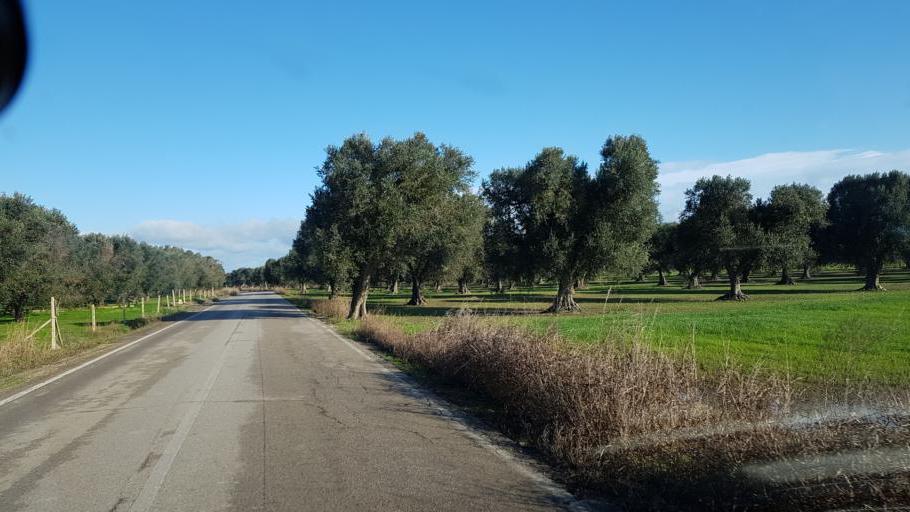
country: IT
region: Apulia
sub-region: Provincia di Brindisi
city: Tuturano
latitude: 40.5627
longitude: 17.9487
